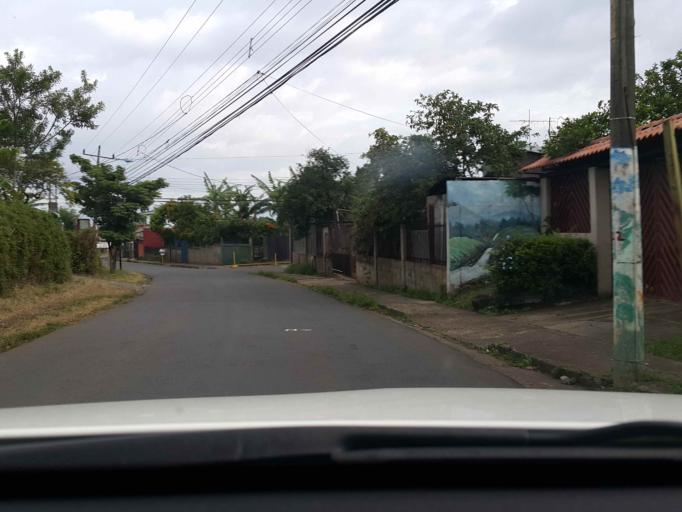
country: CR
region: Heredia
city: San Rafael
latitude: 10.0089
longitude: -84.0961
